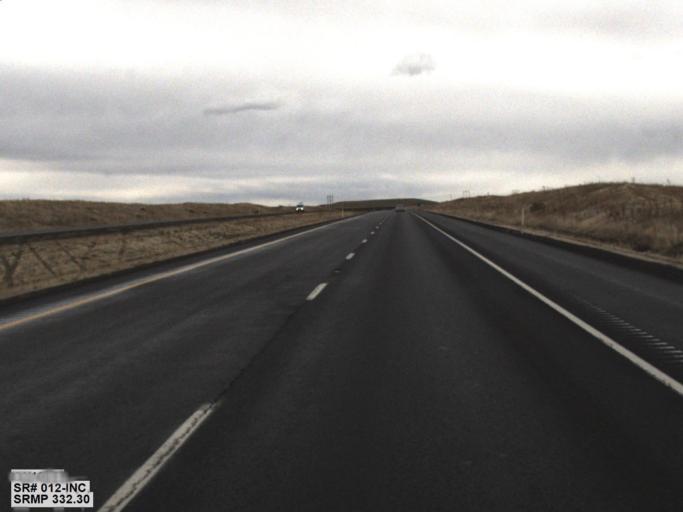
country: US
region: Washington
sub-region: Walla Walla County
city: Garrett
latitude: 46.0637
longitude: -118.4281
